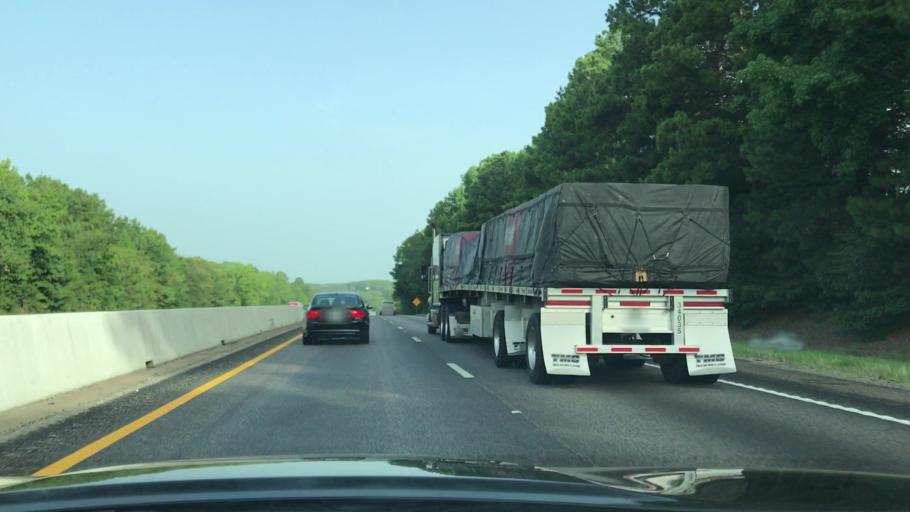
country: US
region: Texas
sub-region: Smith County
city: Lindale
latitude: 32.4640
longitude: -95.3301
